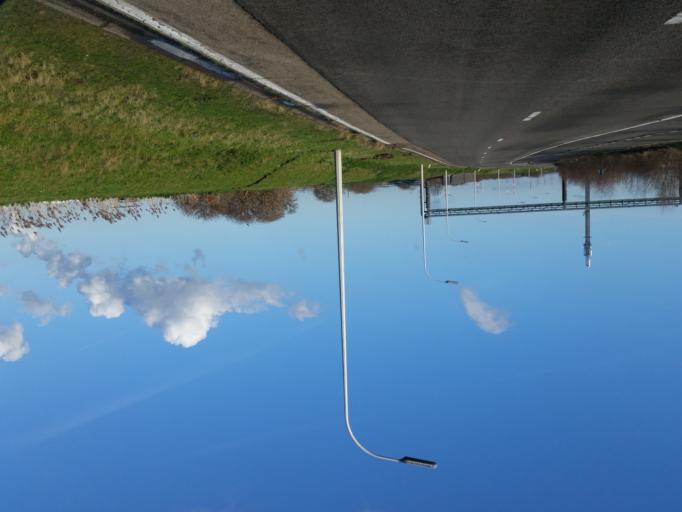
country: BE
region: Flanders
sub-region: Provincie Antwerpen
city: Zwijndrecht
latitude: 51.2477
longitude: 4.3270
